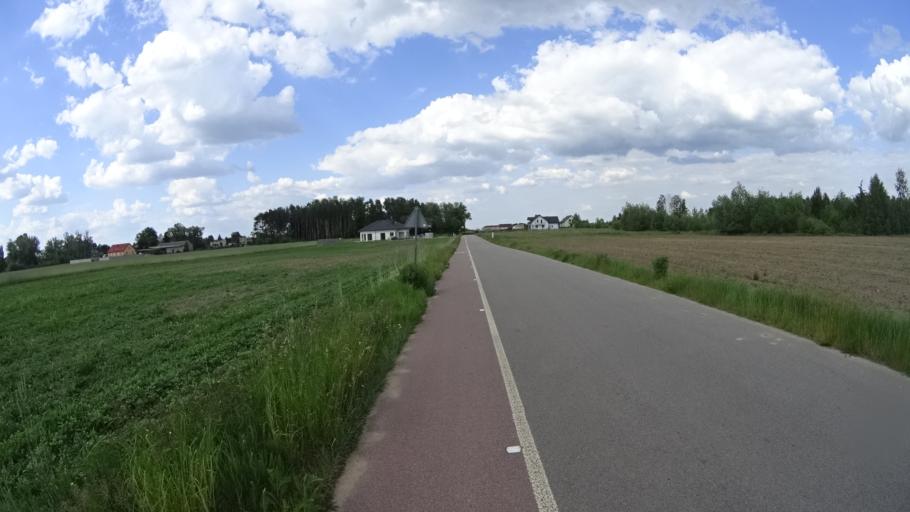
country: PL
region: Masovian Voivodeship
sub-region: Powiat piaseczynski
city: Tarczyn
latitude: 52.0053
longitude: 20.8306
